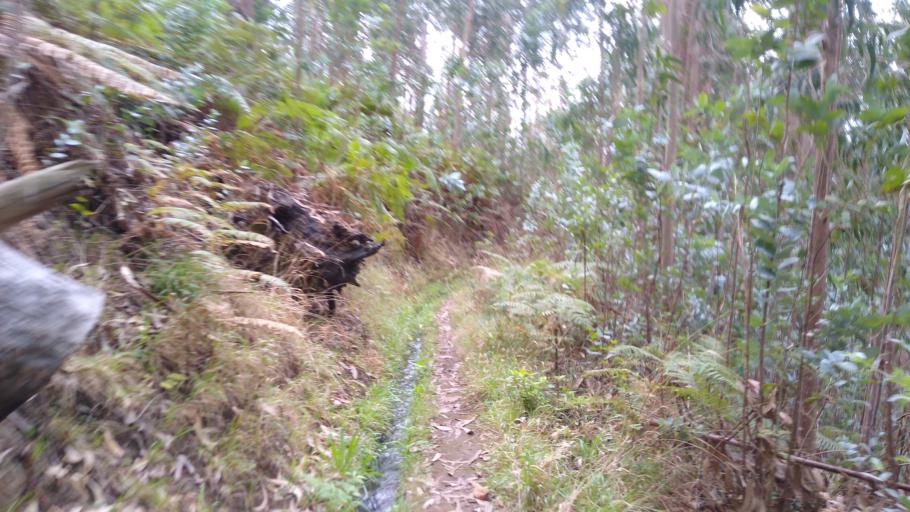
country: PT
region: Madeira
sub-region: Camara de Lobos
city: Curral das Freiras
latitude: 32.6909
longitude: -16.9398
